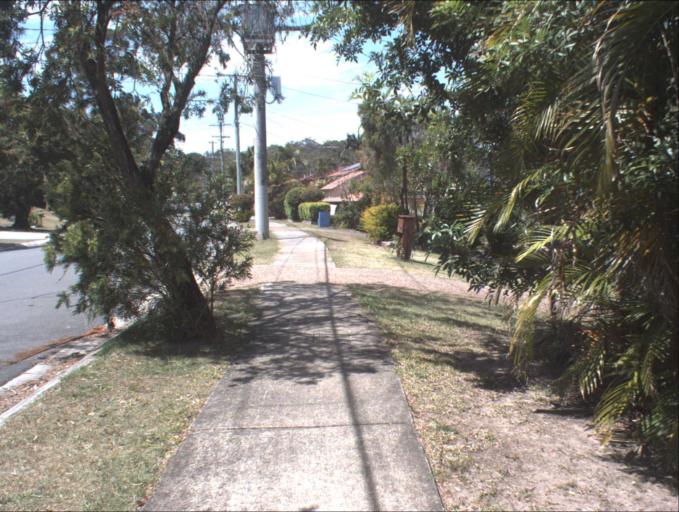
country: AU
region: Queensland
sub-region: Logan
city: Springwood
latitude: -27.5978
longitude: 153.1433
